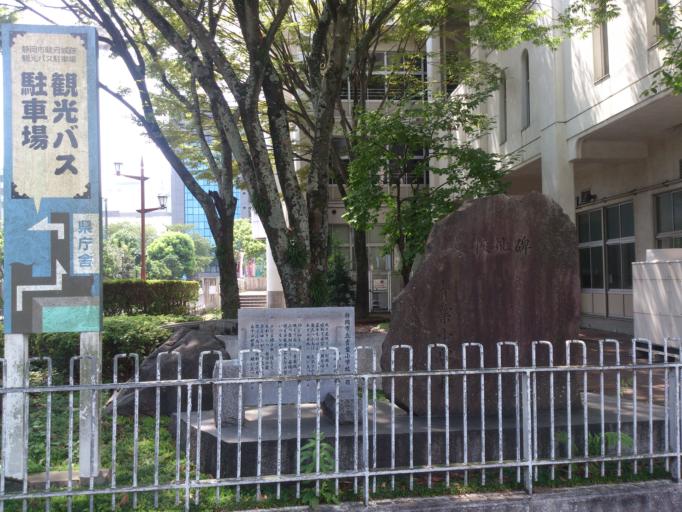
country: JP
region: Shizuoka
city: Shizuoka-shi
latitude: 34.9771
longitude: 138.3851
